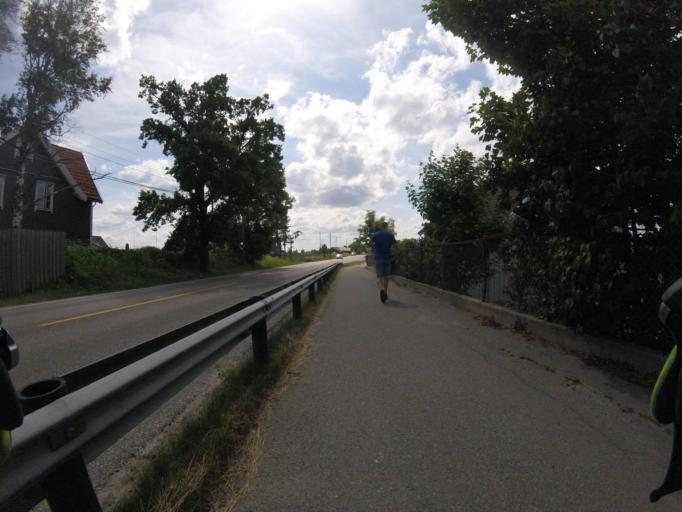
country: NO
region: Akershus
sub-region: Skedsmo
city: Lillestrom
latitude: 59.9770
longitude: 11.0568
